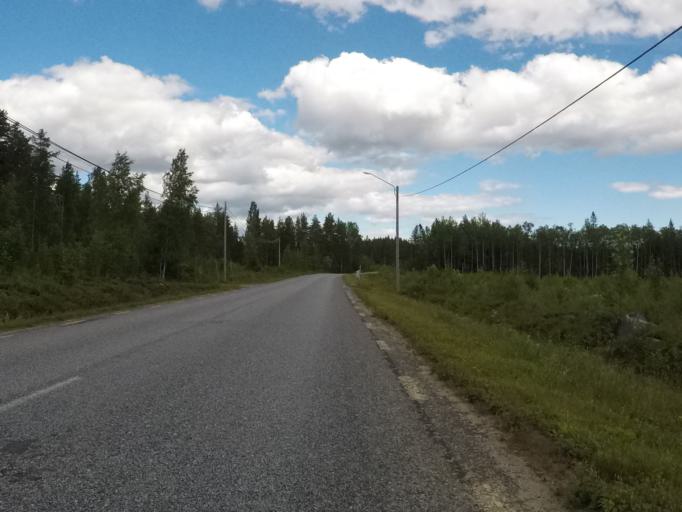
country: SE
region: Vaesterbotten
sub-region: Umea Kommun
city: Saevar
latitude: 63.9215
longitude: 20.7681
